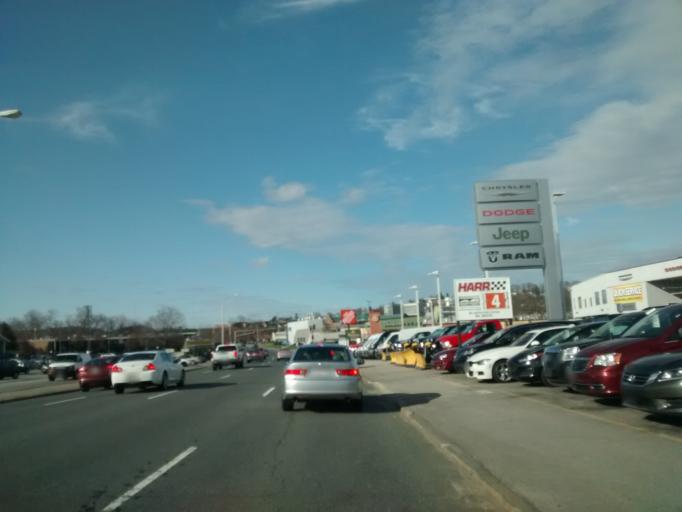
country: US
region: Massachusetts
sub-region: Worcester County
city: Worcester
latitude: 42.2910
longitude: -71.8031
